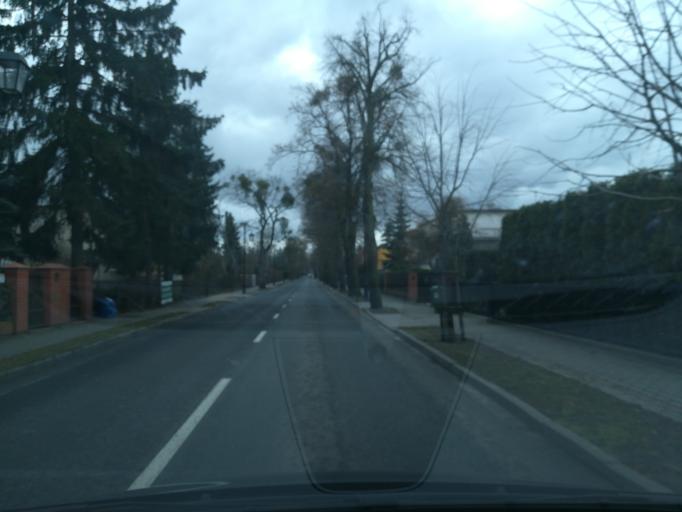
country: PL
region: Kujawsko-Pomorskie
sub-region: Powiat aleksandrowski
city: Ciechocinek
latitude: 52.8776
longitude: 18.7808
